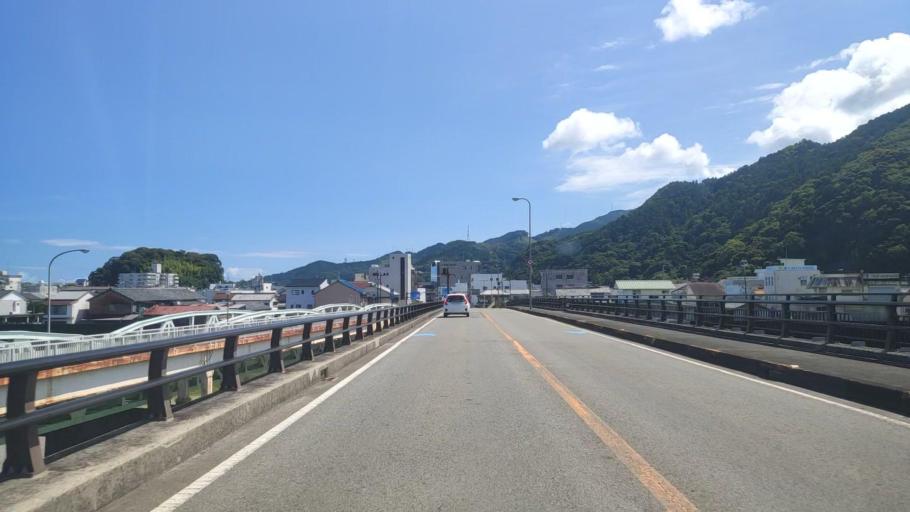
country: JP
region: Wakayama
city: Shingu
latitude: 33.7324
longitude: 135.9874
